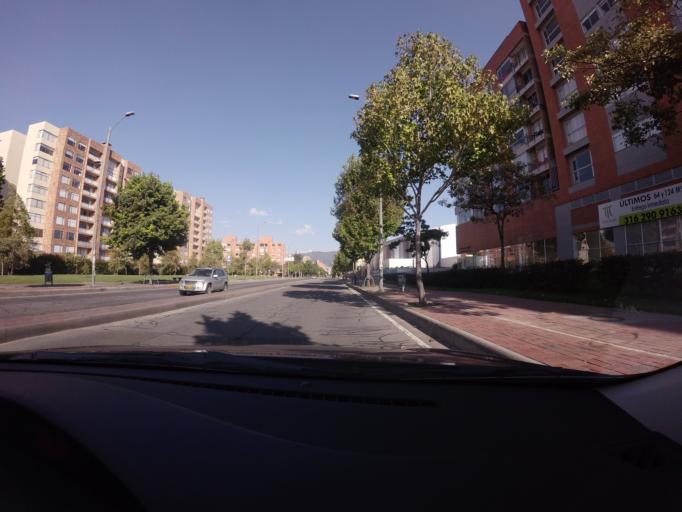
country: CO
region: Bogota D.C.
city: Barrio San Luis
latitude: 4.7257
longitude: -74.0705
